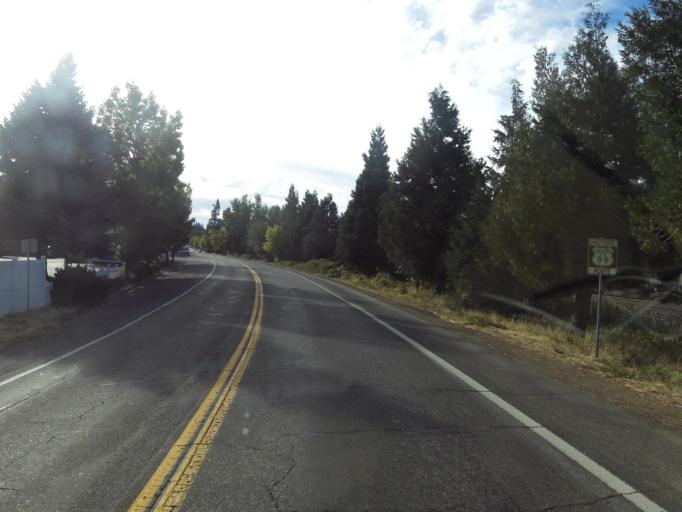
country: US
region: California
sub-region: Siskiyou County
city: Mount Shasta
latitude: 41.3177
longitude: -122.3180
